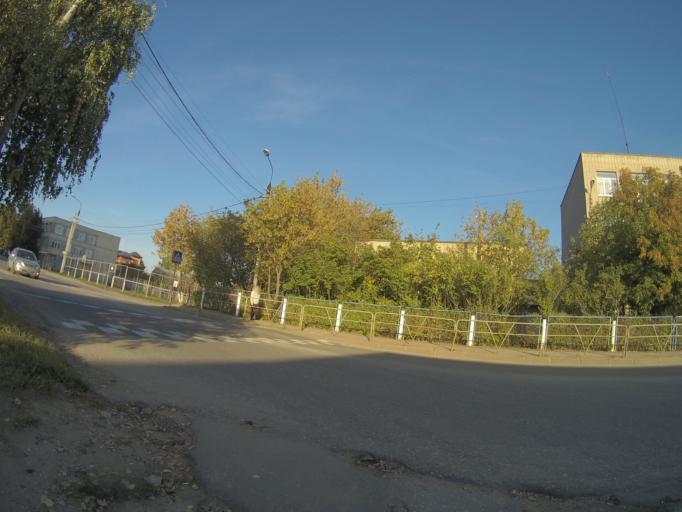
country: RU
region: Vladimir
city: Vladimir
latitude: 56.1123
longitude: 40.3734
